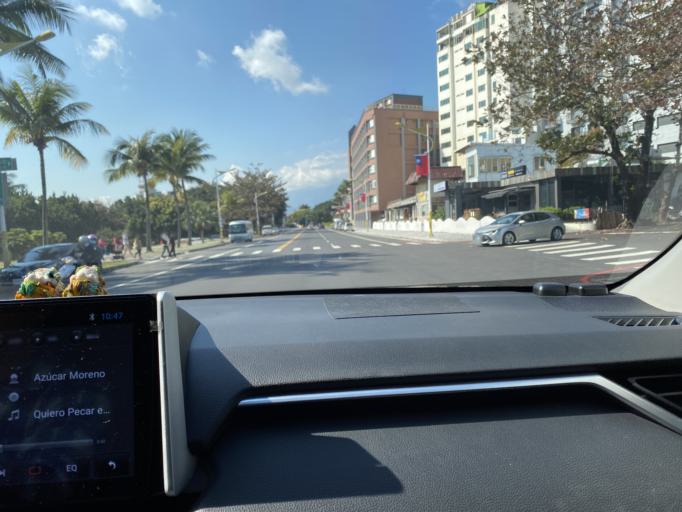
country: TW
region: Taiwan
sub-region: Hualien
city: Hualian
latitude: 23.9827
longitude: 121.6225
